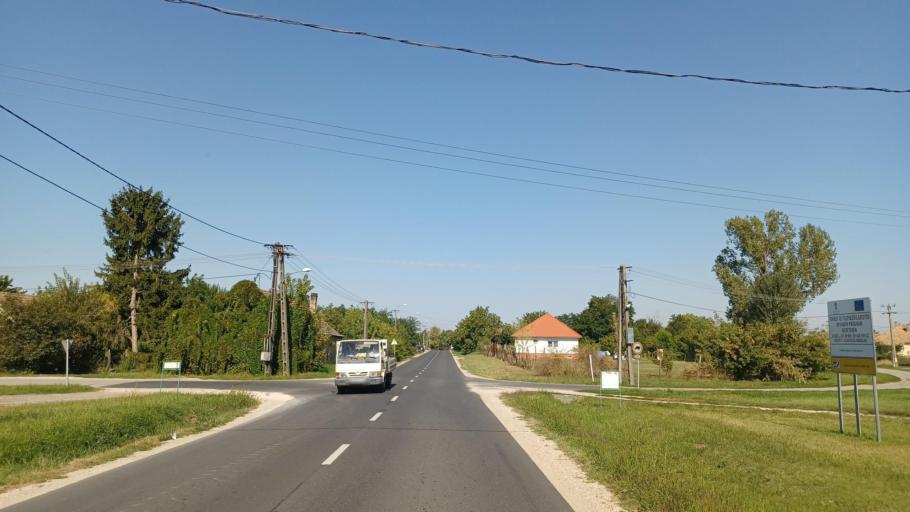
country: HU
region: Fejer
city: Cece
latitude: 46.7639
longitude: 18.6418
